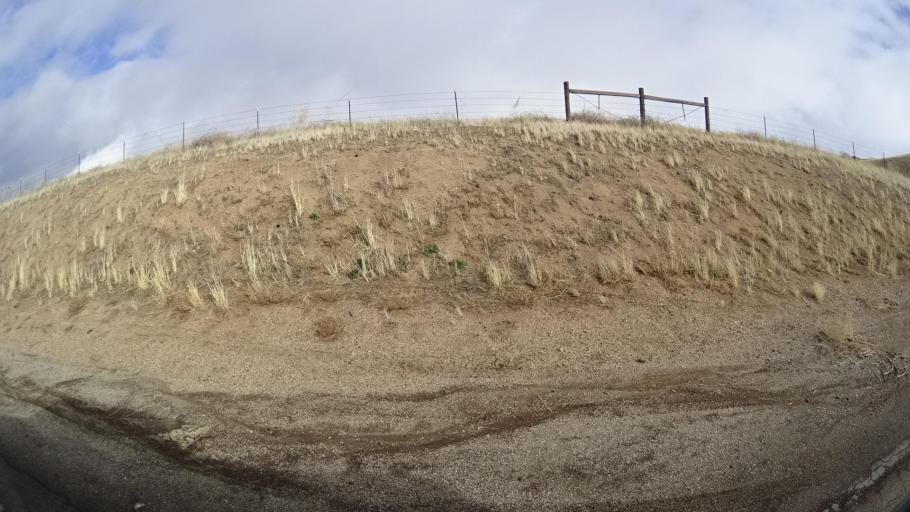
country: US
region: California
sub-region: Kern County
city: Maricopa
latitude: 34.9047
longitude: -119.3785
